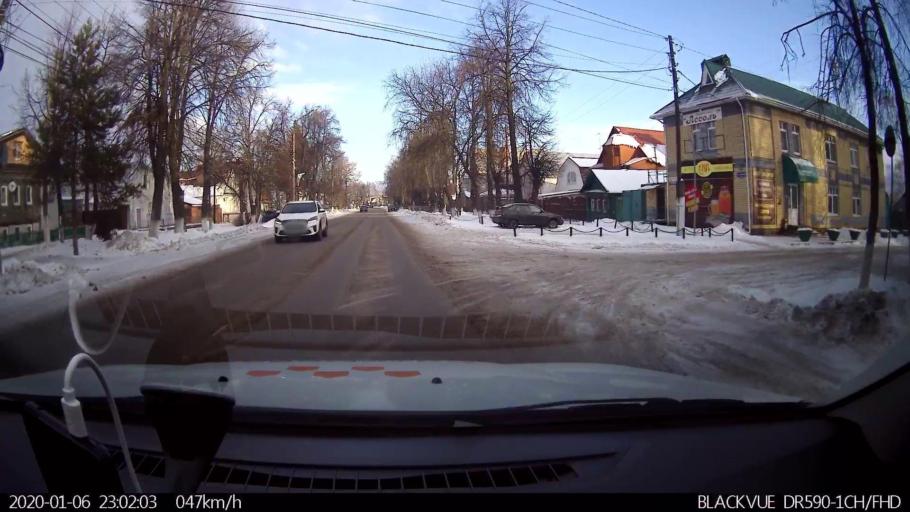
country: RU
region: Nizjnij Novgorod
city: Bogorodsk
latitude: 56.1077
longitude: 43.5252
